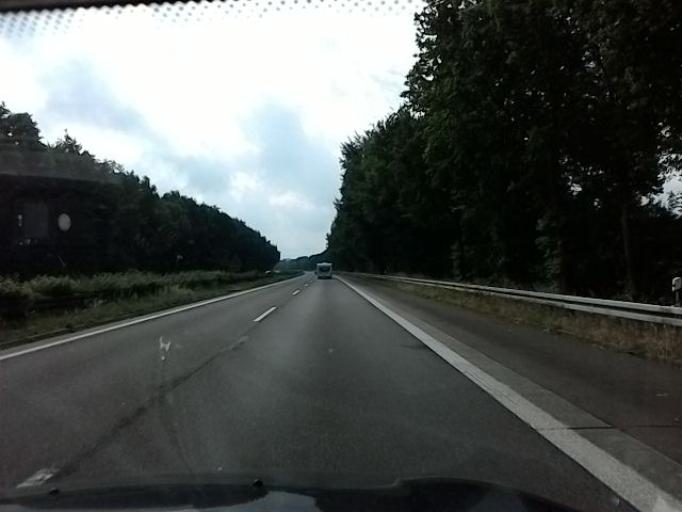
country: DE
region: North Rhine-Westphalia
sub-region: Regierungsbezirk Dusseldorf
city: Wesel
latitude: 51.6941
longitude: 6.6714
